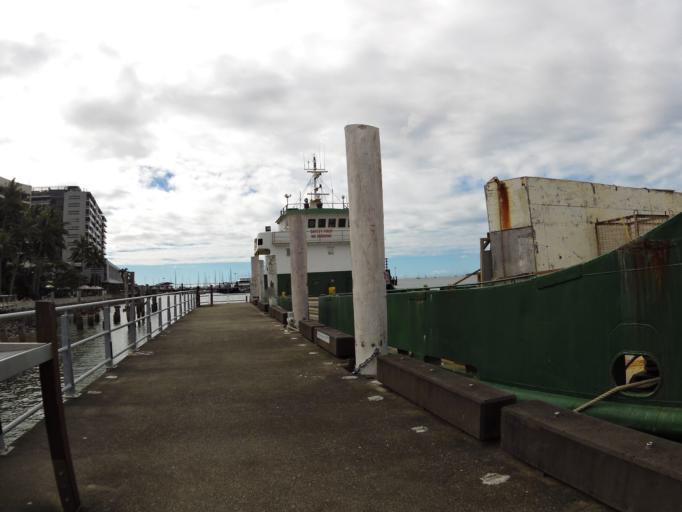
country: AU
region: Queensland
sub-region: Cairns
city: Cairns
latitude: -16.9240
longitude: 145.7809
